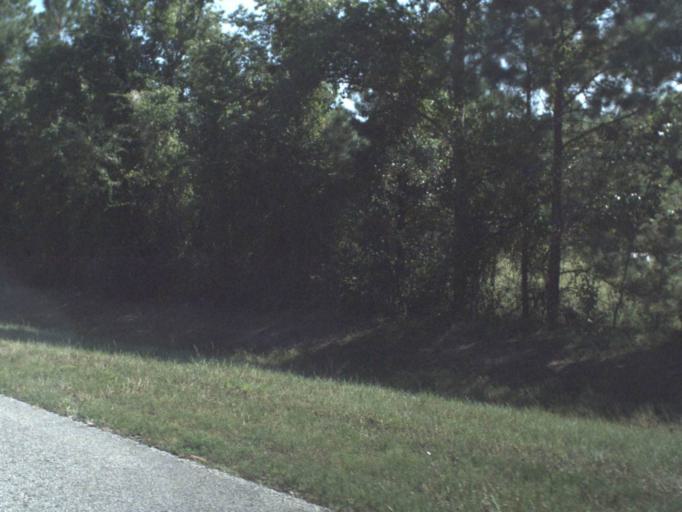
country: US
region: Florida
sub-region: Alachua County
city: Hawthorne
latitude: 29.6820
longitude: -82.1245
